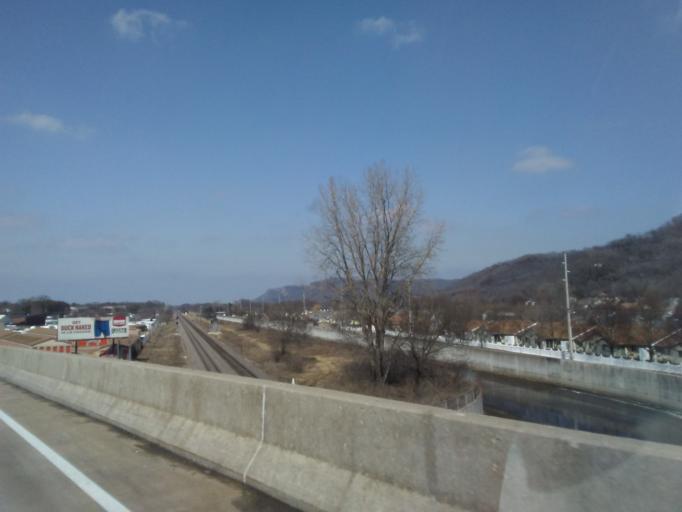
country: US
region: Wisconsin
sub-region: La Crosse County
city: La Crosse
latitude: 43.7619
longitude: -91.2075
